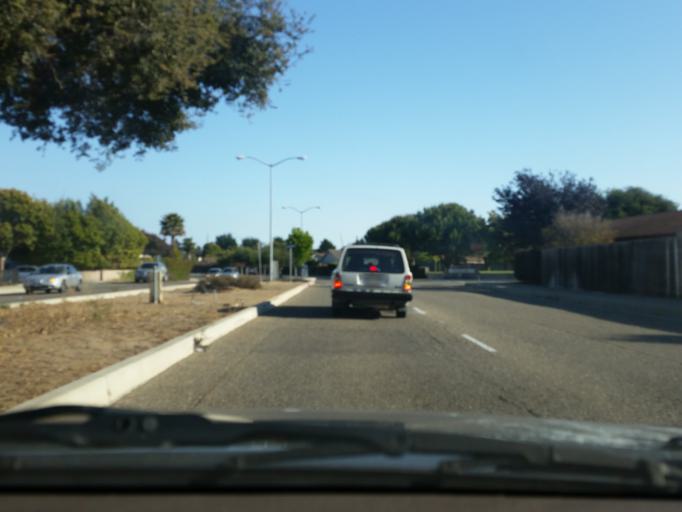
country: US
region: California
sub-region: San Luis Obispo County
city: Grover Beach
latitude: 35.1155
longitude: -120.6096
